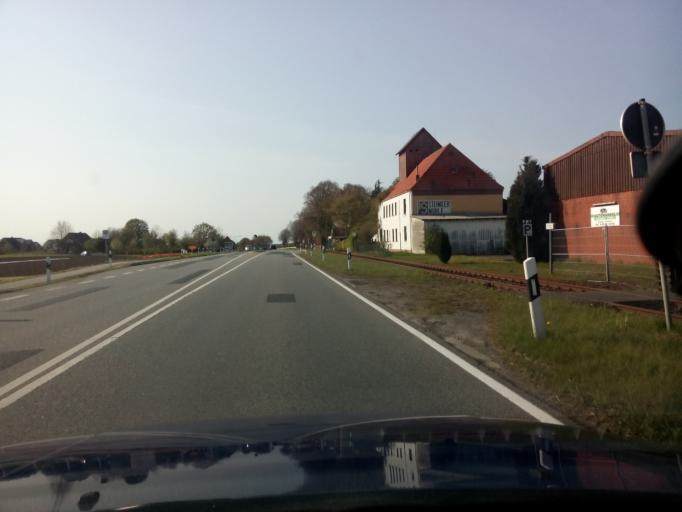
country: DE
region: Lower Saxony
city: Syke
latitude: 52.9024
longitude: 8.8418
